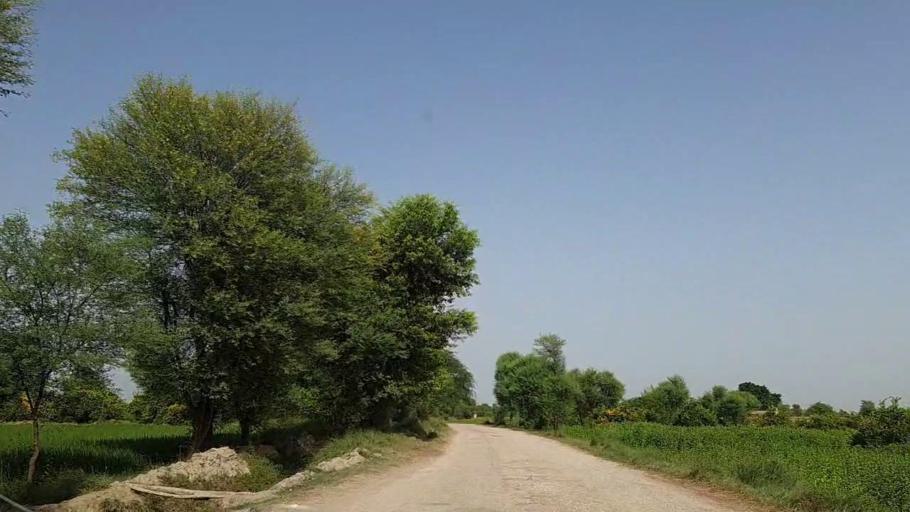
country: PK
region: Sindh
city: Kandiaro
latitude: 27.0653
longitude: 68.1850
